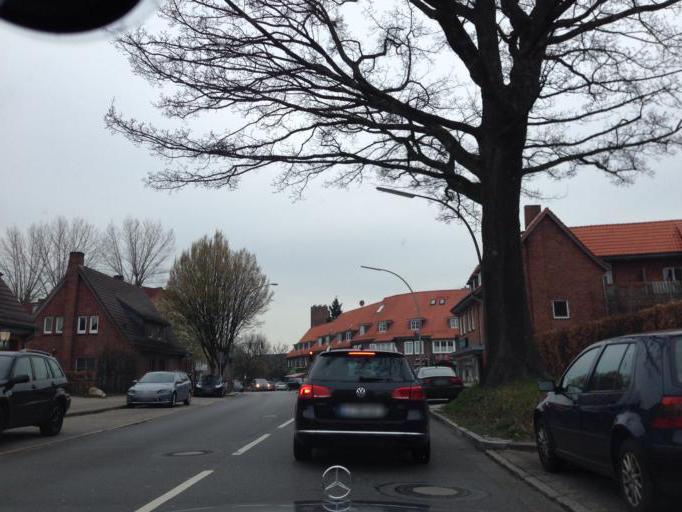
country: DE
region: Hamburg
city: Sasel
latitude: 53.6527
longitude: 10.1141
